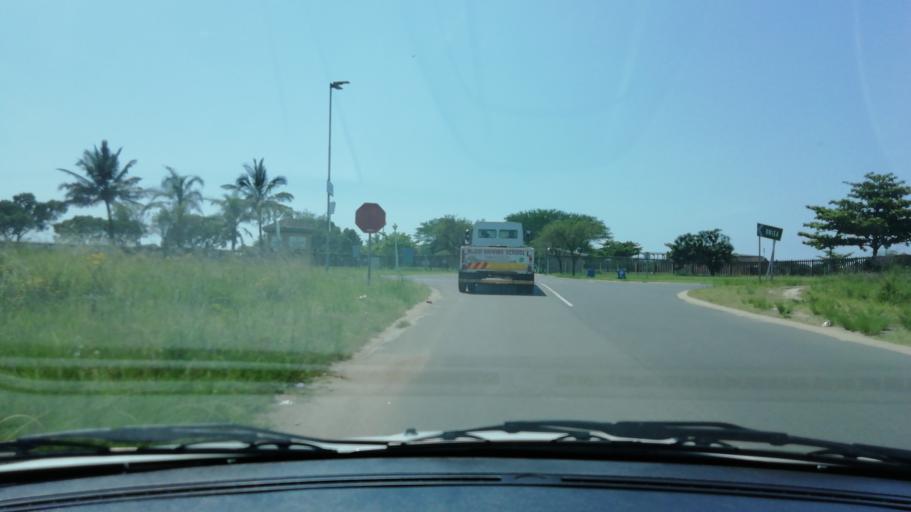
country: ZA
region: KwaZulu-Natal
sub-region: uThungulu District Municipality
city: Richards Bay
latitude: -28.7423
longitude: 32.0518
